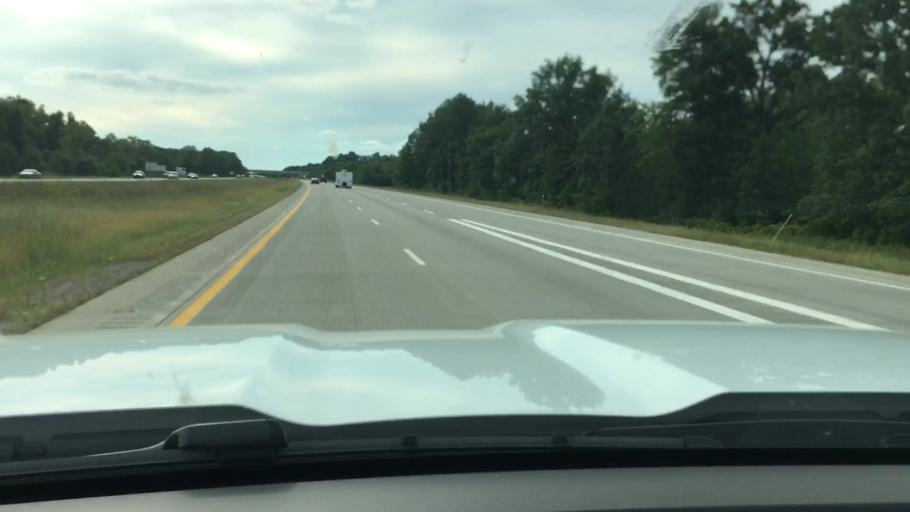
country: US
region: Michigan
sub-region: Lapeer County
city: Lapeer
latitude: 43.0319
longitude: -83.3668
